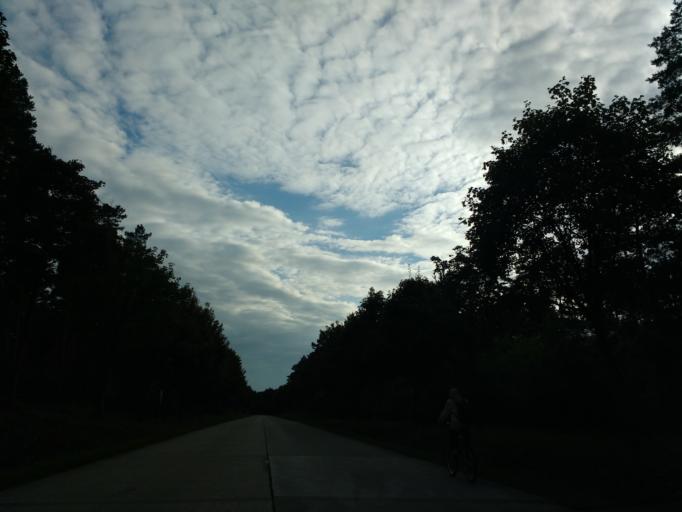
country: DE
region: North Rhine-Westphalia
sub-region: Regierungsbezirk Detmold
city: Augustdorf
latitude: 51.8695
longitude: 8.6983
